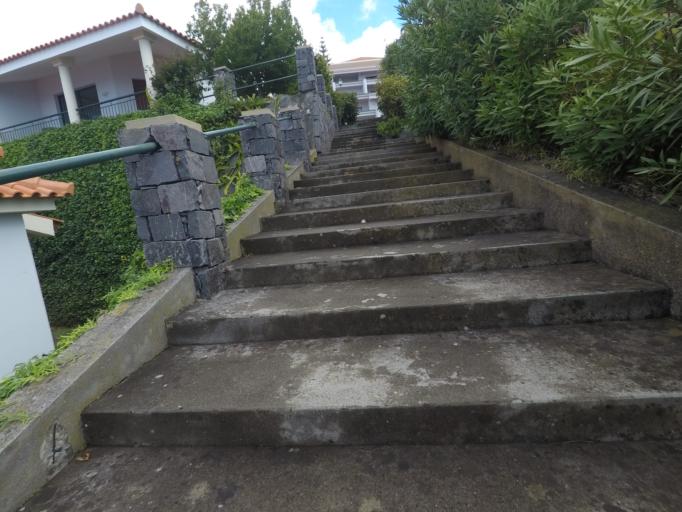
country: PT
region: Madeira
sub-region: Calheta
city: Faja da Ovelha
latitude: 32.7519
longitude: -17.2177
